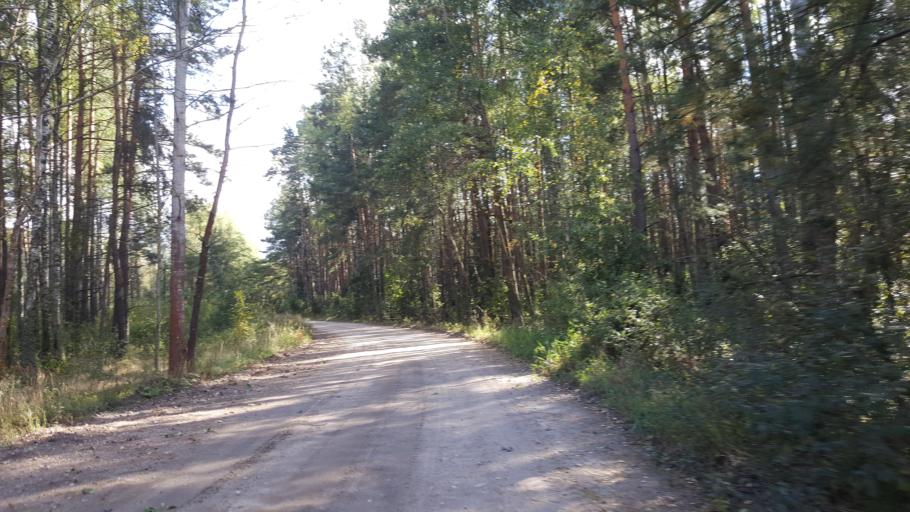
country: BY
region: Brest
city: Kamyanyets
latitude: 52.4322
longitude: 23.9438
